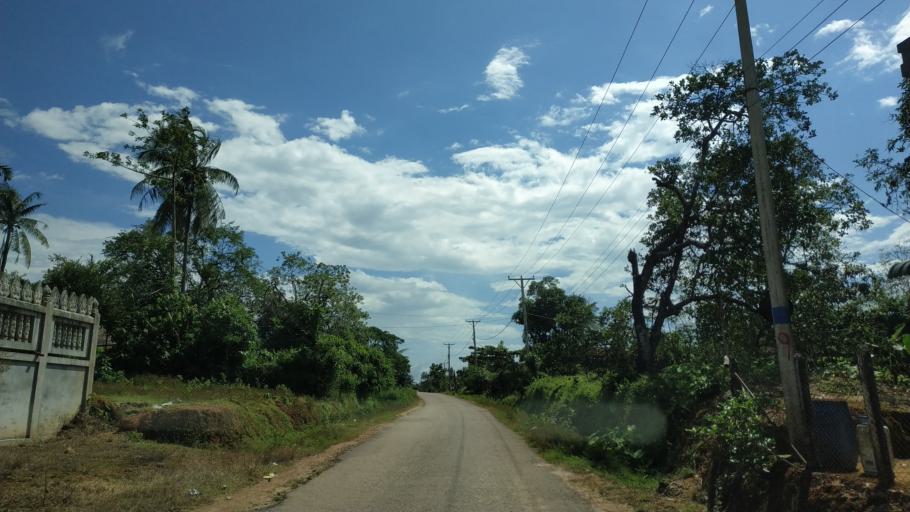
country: MM
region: Tanintharyi
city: Dawei
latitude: 14.2184
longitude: 98.1943
